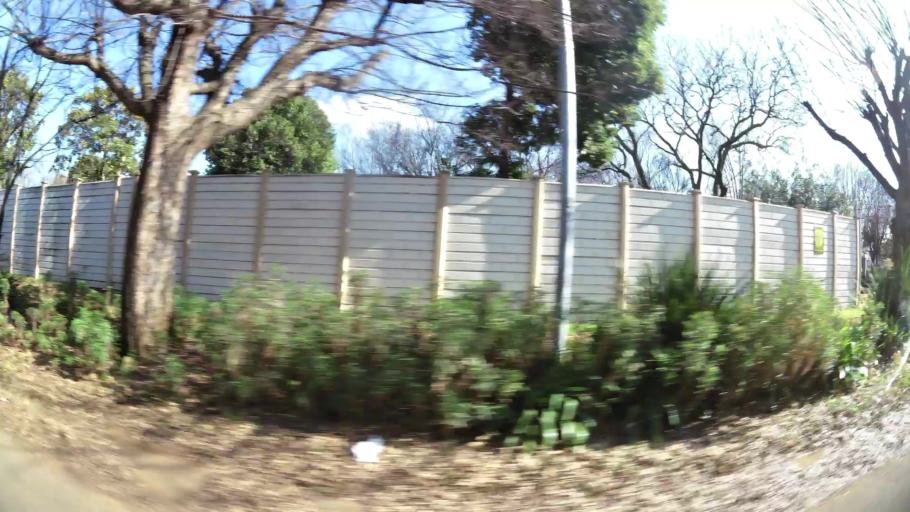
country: ZA
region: Gauteng
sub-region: Ekurhuleni Metropolitan Municipality
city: Benoni
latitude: -26.1535
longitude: 28.3351
